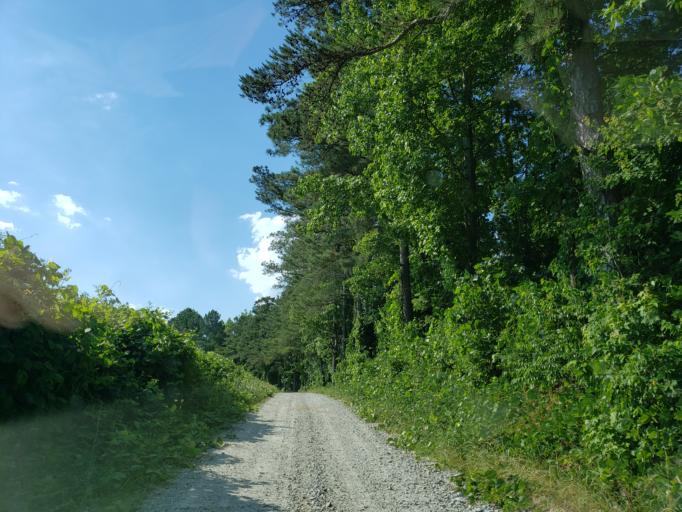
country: US
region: Georgia
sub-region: Haralson County
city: Buchanan
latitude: 33.8089
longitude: -85.1029
